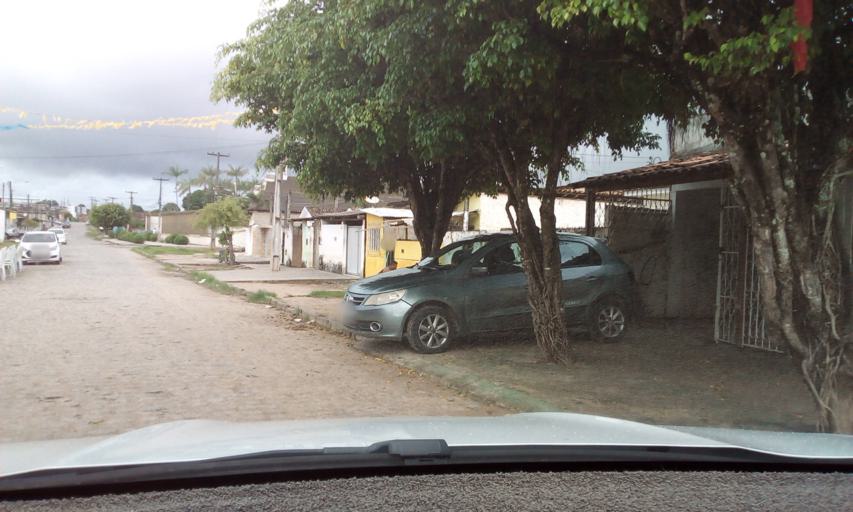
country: BR
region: Paraiba
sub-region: Bayeux
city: Bayeux
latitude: -7.1536
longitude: -34.9031
